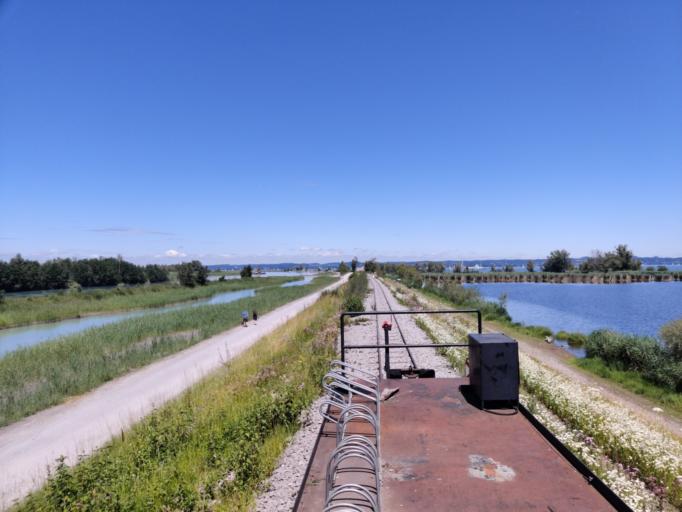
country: AT
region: Vorarlberg
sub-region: Politischer Bezirk Bregenz
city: Hard
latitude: 47.4941
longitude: 9.6720
